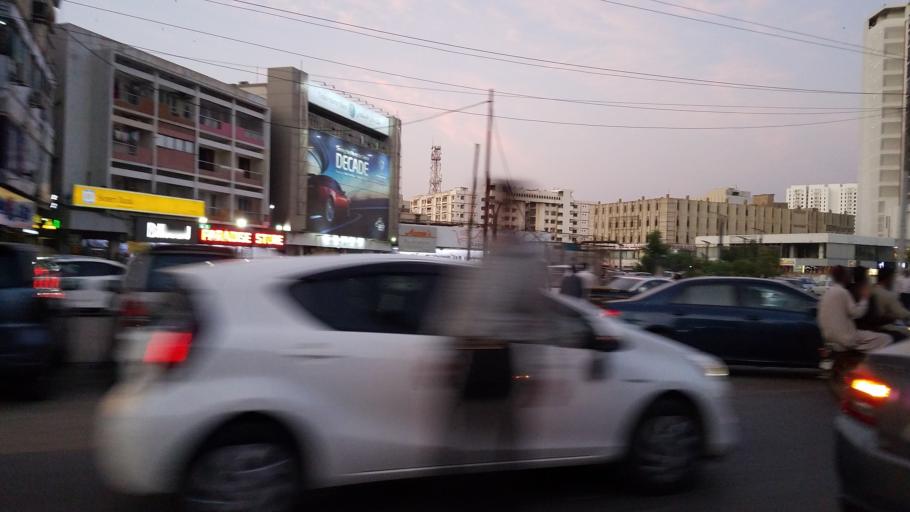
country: PK
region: Sindh
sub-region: Karachi District
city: Karachi
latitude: 24.8278
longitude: 67.0339
